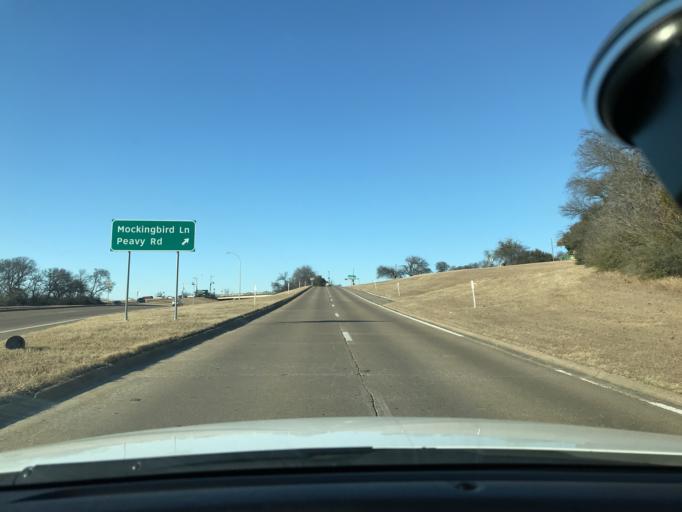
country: US
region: Texas
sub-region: Dallas County
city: Highland Park
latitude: 32.8510
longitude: -96.7163
